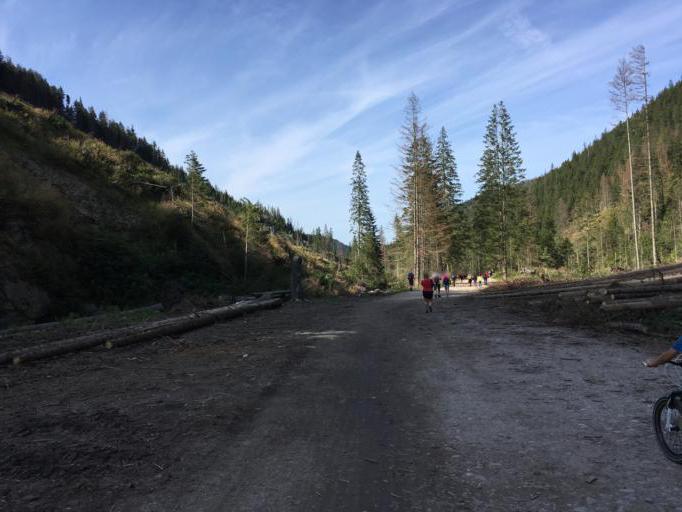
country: PL
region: Lesser Poland Voivodeship
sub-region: Powiat tatrzanski
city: Koscielisko
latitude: 49.2483
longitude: 19.8141
